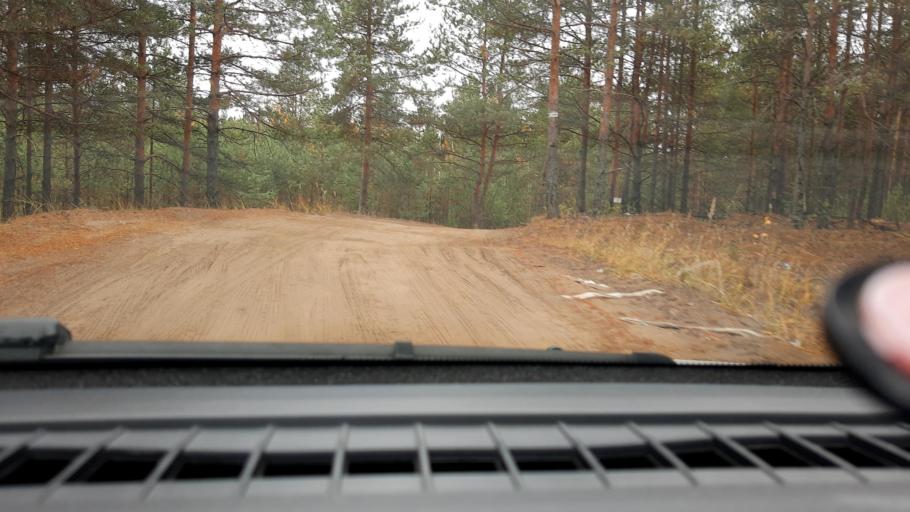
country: RU
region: Nizjnij Novgorod
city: Lukino
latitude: 56.3865
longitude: 43.6485
